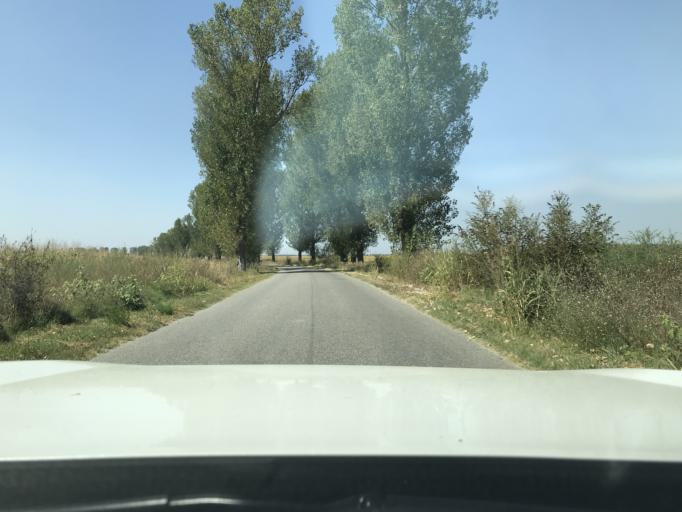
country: RO
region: Olt
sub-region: Comuna Falcoiu
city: Falcoiu
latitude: 44.2363
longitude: 24.3591
